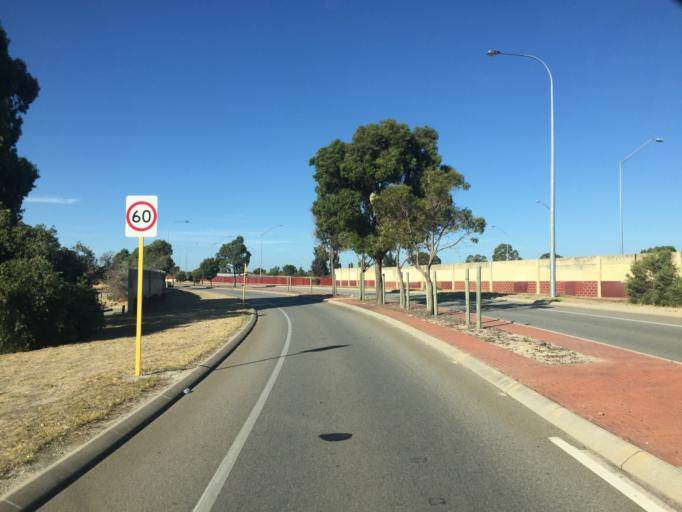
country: AU
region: Western Australia
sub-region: Canning
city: East Cannington
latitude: -32.0079
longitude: 115.9721
